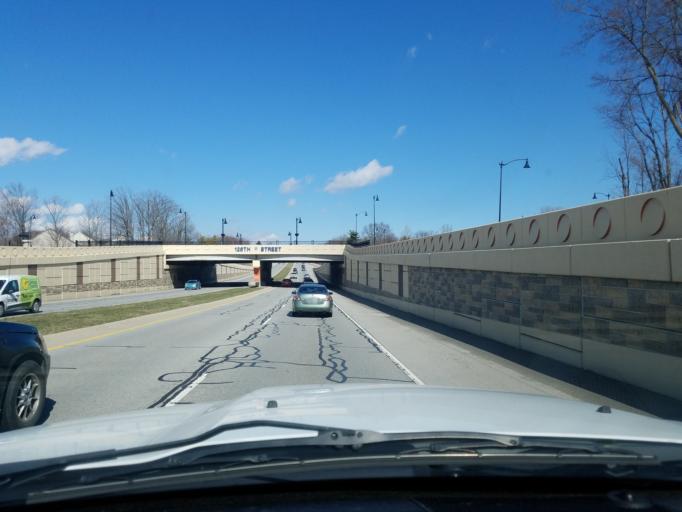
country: US
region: Indiana
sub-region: Hamilton County
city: Carmel
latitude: 39.9701
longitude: -86.1126
